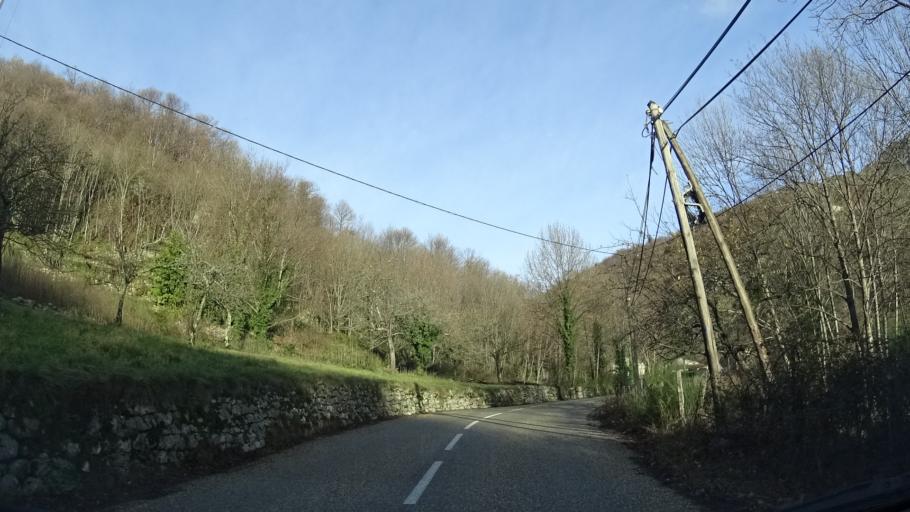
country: FR
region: Rhone-Alpes
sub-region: Departement de l'Ardeche
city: Thueyts
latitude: 44.7253
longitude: 4.2597
